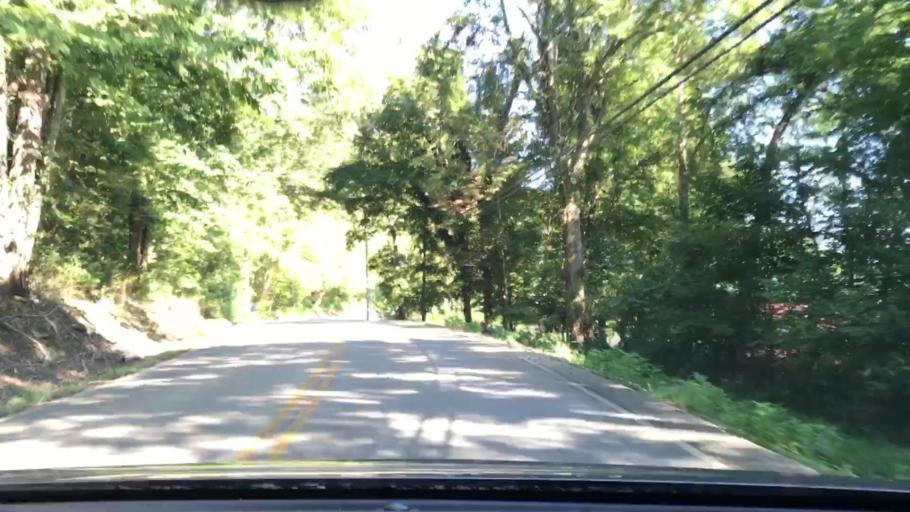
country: US
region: Tennessee
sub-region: Smith County
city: Carthage
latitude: 36.3070
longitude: -85.9508
